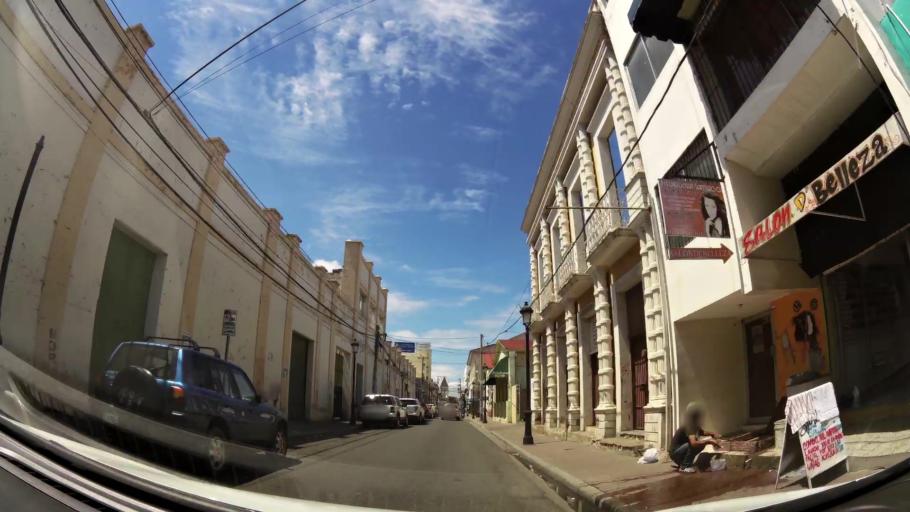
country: DO
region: Santiago
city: Santiago de los Caballeros
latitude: 19.4497
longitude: -70.7031
